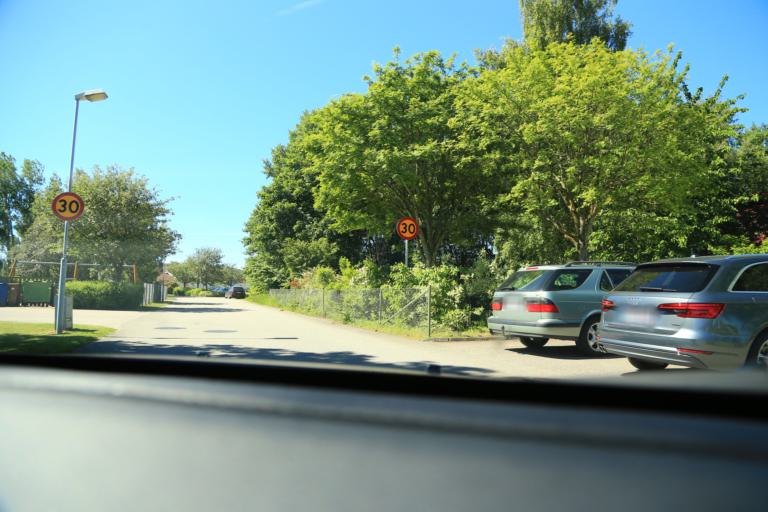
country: SE
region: Halland
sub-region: Varbergs Kommun
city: Varberg
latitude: 57.1171
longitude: 12.2738
